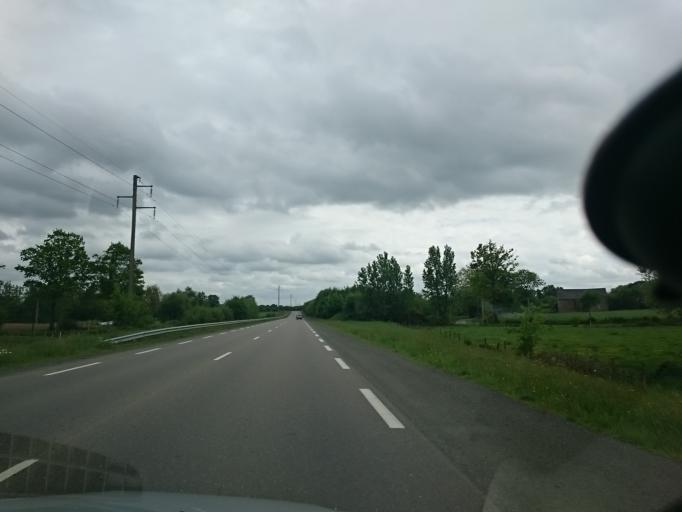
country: FR
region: Brittany
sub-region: Departement d'Ille-et-Vilaine
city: Saint-Brice-en-Cogles
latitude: 48.4068
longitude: -1.3808
